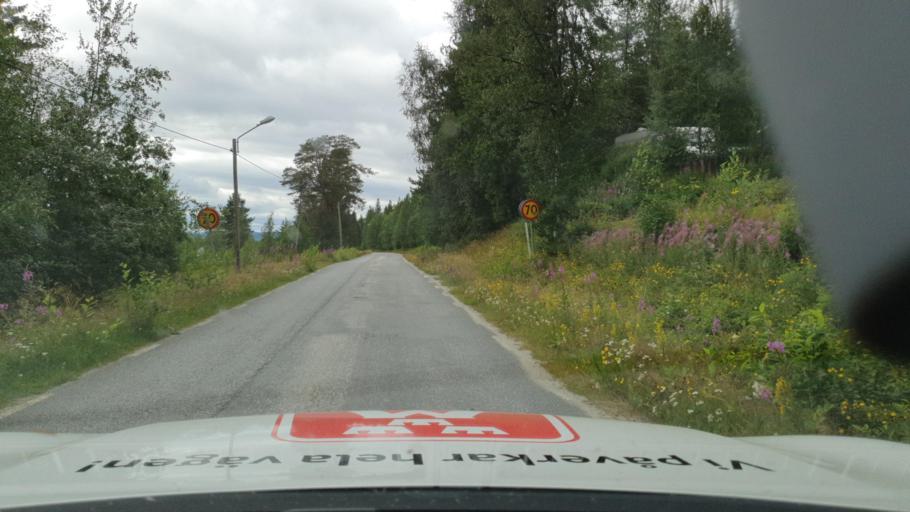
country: SE
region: Vaesterbotten
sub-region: Dorotea Kommun
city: Dorotea
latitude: 64.1874
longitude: 16.6474
